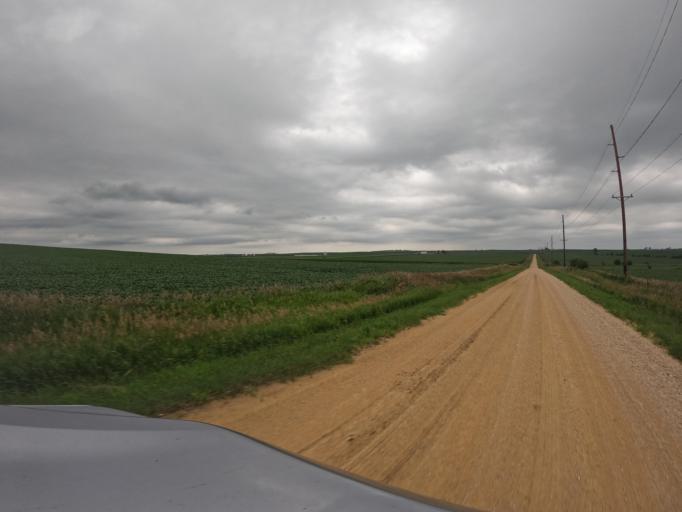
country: US
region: Iowa
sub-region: Clinton County
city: De Witt
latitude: 41.9382
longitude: -90.5984
